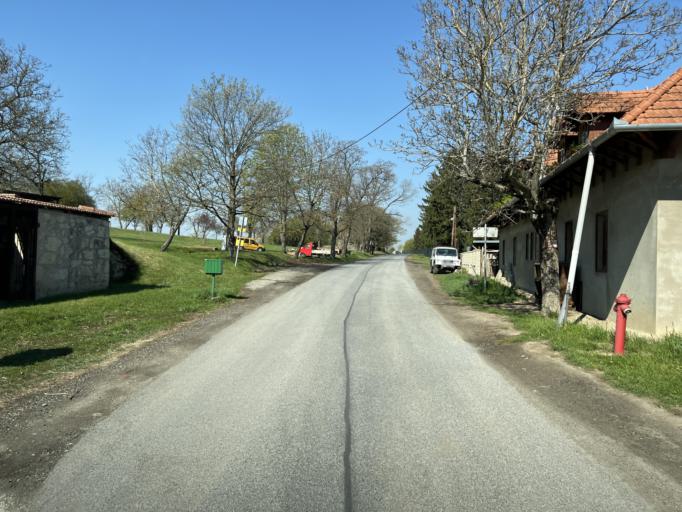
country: HU
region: Pest
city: Szob
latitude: 47.9359
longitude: 18.8203
